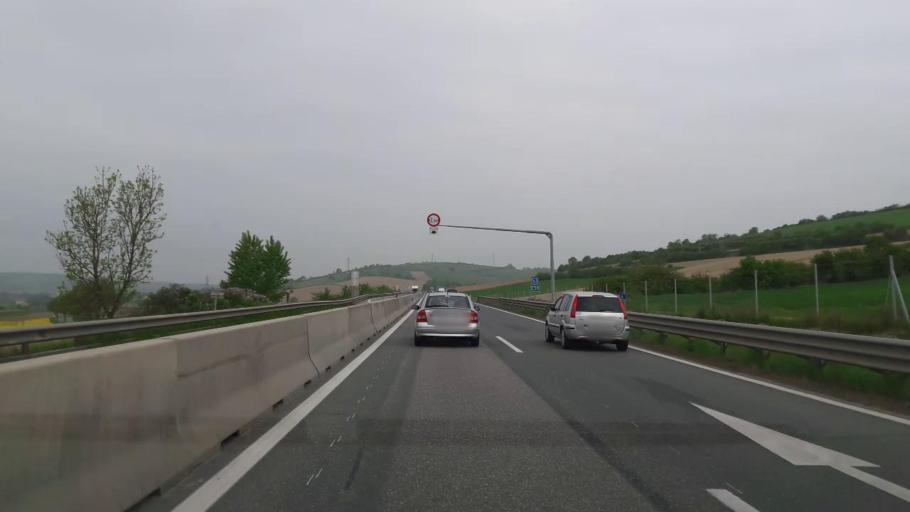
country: AT
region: Lower Austria
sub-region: Politischer Bezirk Hollabrunn
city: Gollersdorf
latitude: 48.5074
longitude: 16.0963
